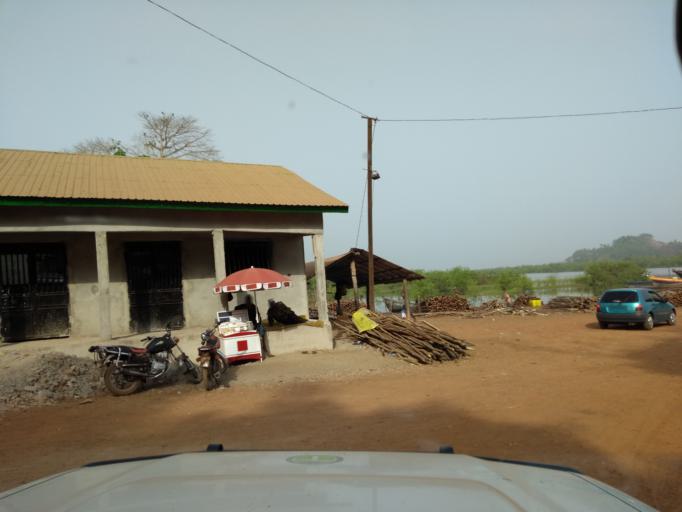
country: GN
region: Kindia
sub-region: Prefecture de Dubreka
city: Dubreka
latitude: 9.7930
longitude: -13.5249
